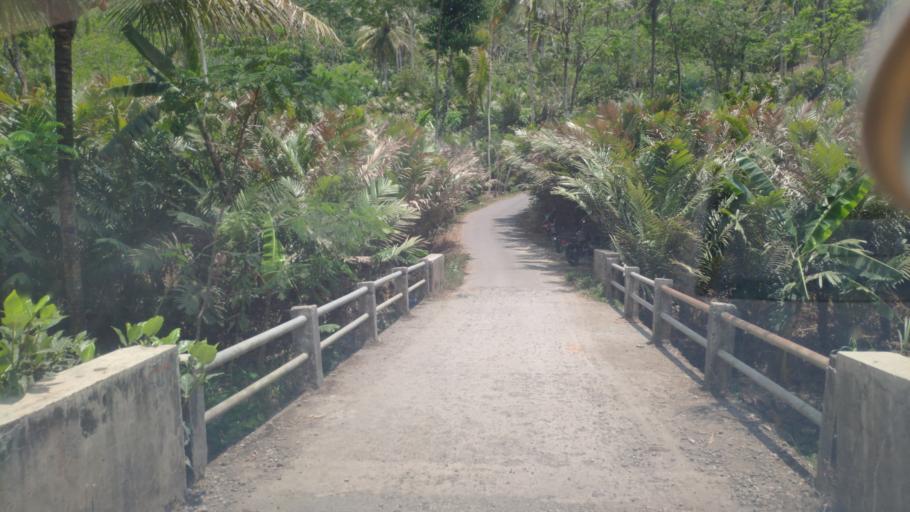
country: ID
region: Central Java
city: Wonosobo
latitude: -7.3334
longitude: 109.6735
